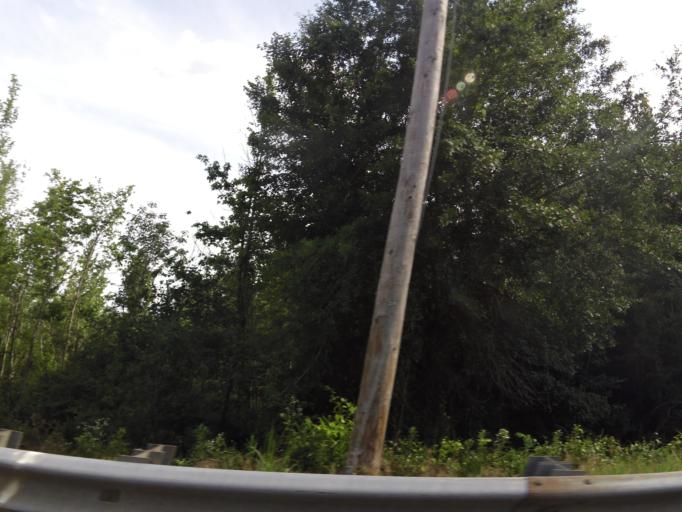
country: US
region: Tennessee
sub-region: Carroll County
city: Bruceton
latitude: 36.0367
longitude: -88.2264
